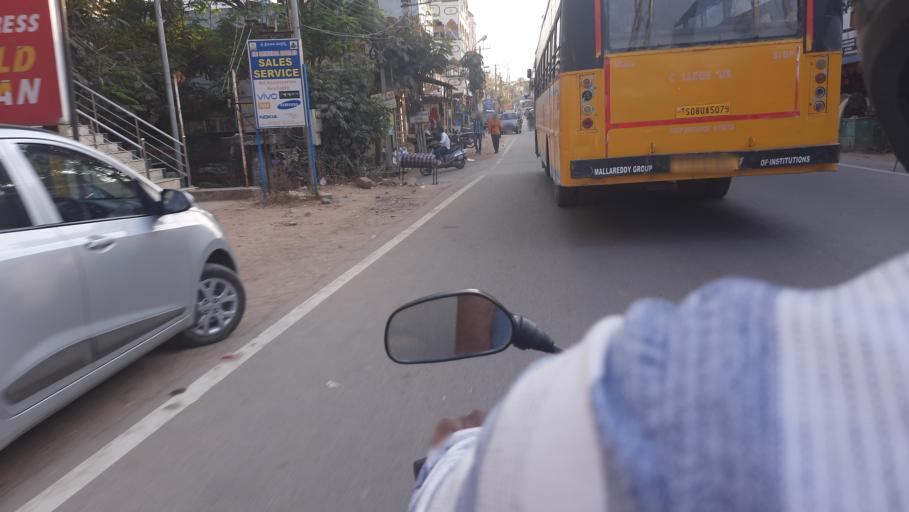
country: IN
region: Telangana
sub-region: Rangareddi
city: Secunderabad
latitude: 17.5043
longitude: 78.5400
